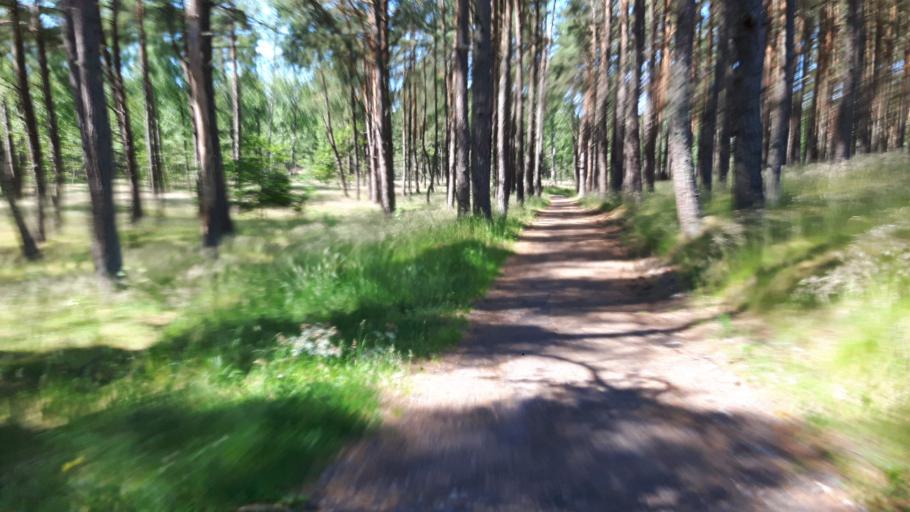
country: LT
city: Neringa
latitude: 55.4132
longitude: 21.0844
